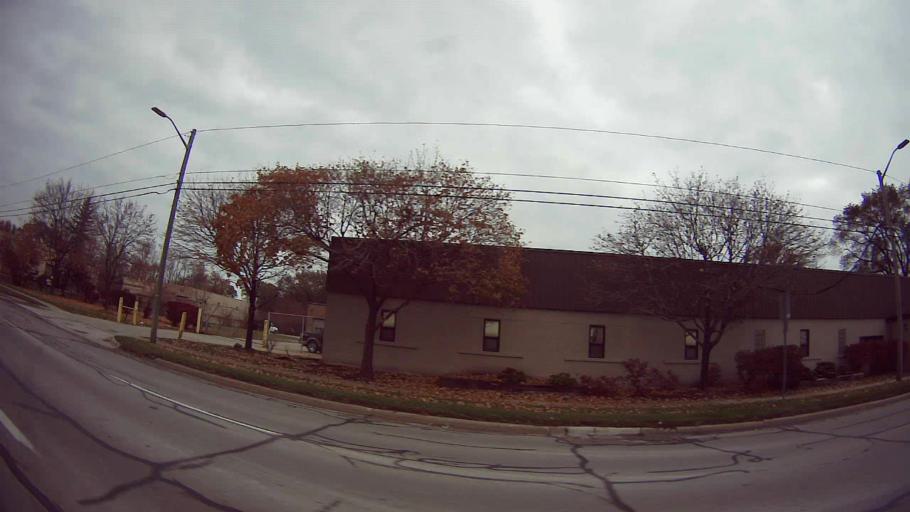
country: US
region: Michigan
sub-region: Macomb County
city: Eastpointe
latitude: 42.4701
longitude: -82.9871
